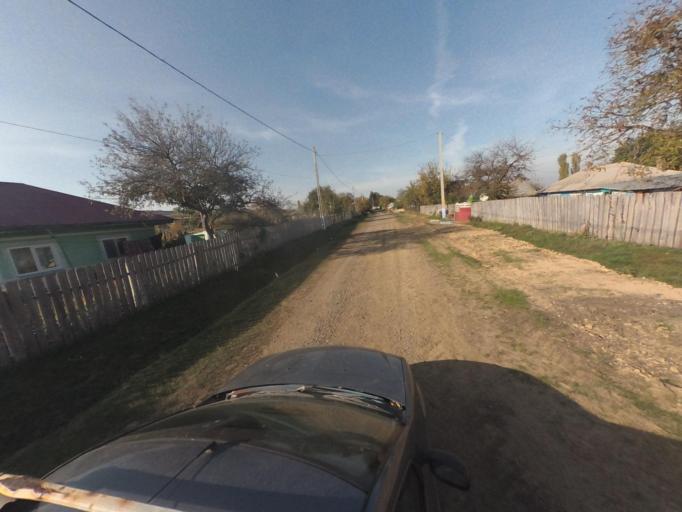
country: RO
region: Vaslui
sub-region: Comuna Bacesti
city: Bacesti
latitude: 46.8741
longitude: 27.1963
